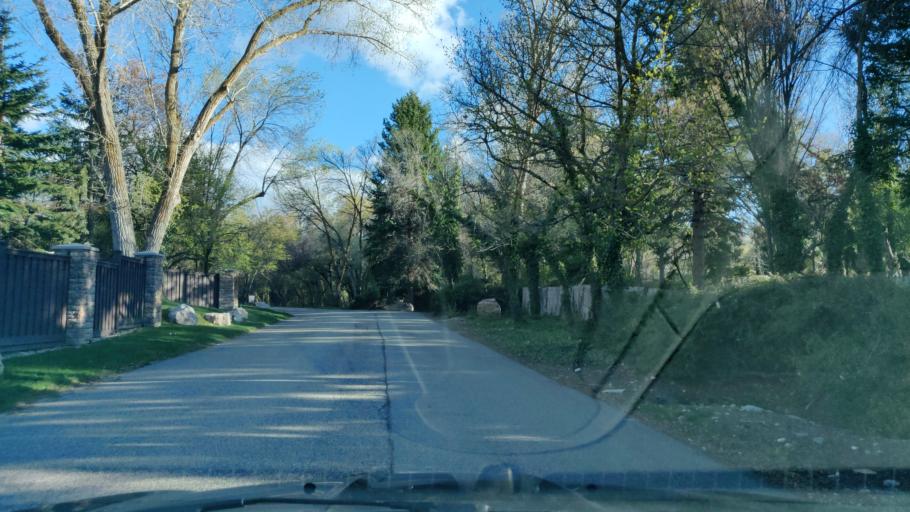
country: US
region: Utah
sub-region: Salt Lake County
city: Cottonwood Heights
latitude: 40.6423
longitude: -111.8198
